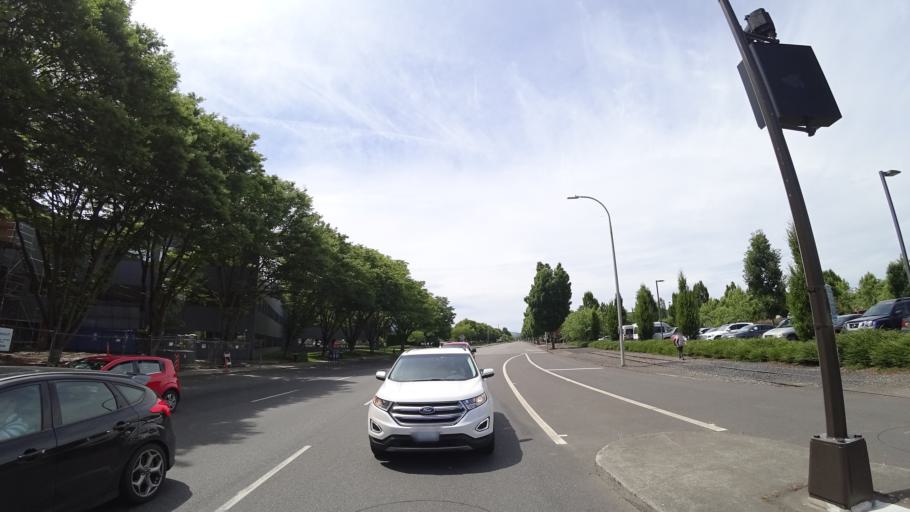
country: US
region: Oregon
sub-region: Multnomah County
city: Portland
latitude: 45.5567
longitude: -122.7052
